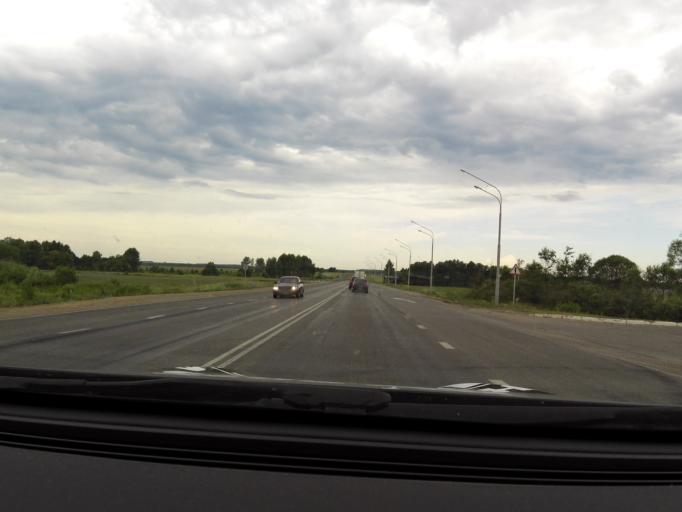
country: RU
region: Bashkortostan
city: Kudeyevskiy
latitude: 54.8168
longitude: 56.7329
